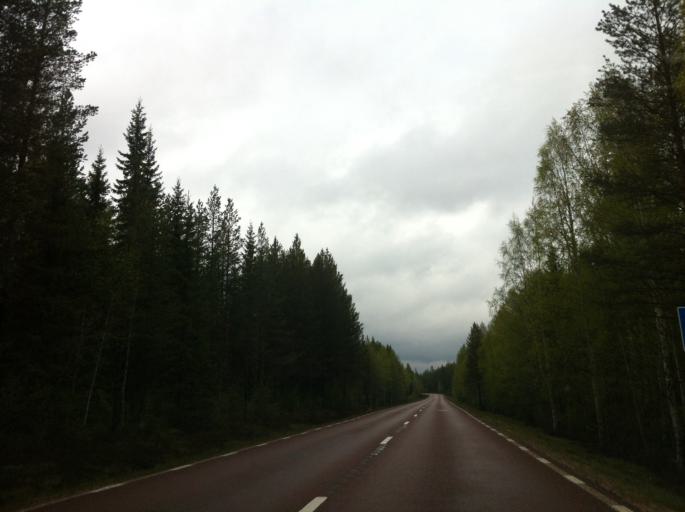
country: SE
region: Jaemtland
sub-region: Harjedalens Kommun
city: Sveg
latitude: 61.8820
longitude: 14.6276
